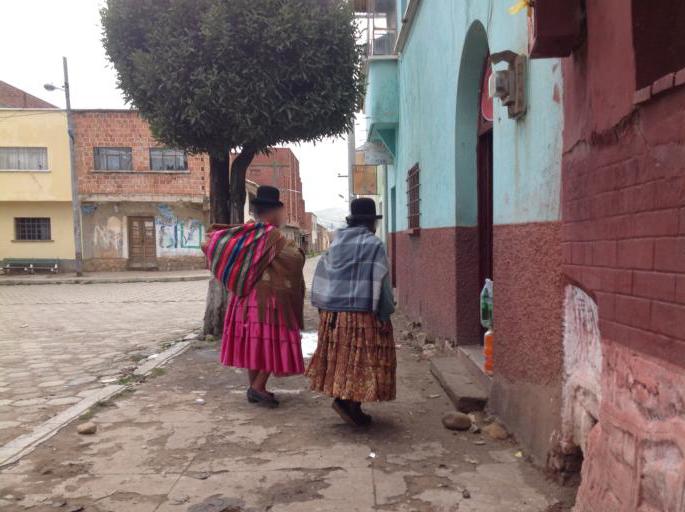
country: BO
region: La Paz
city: Yumani
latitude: -15.7580
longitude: -69.0641
